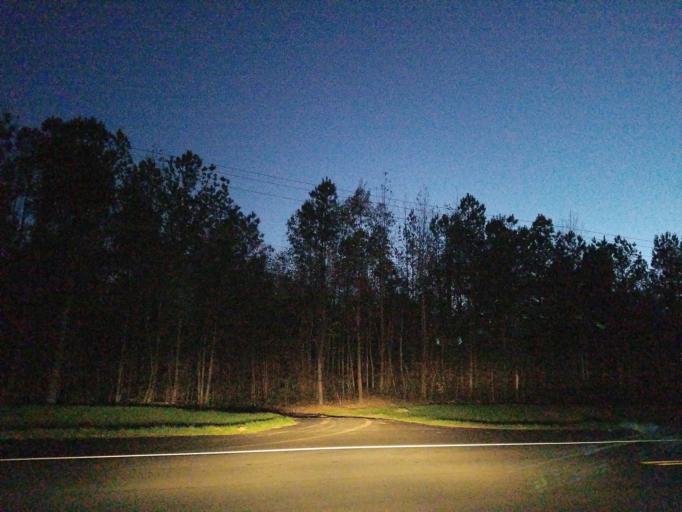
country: US
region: Georgia
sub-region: Forsyth County
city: Cumming
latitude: 34.2510
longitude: -84.1003
